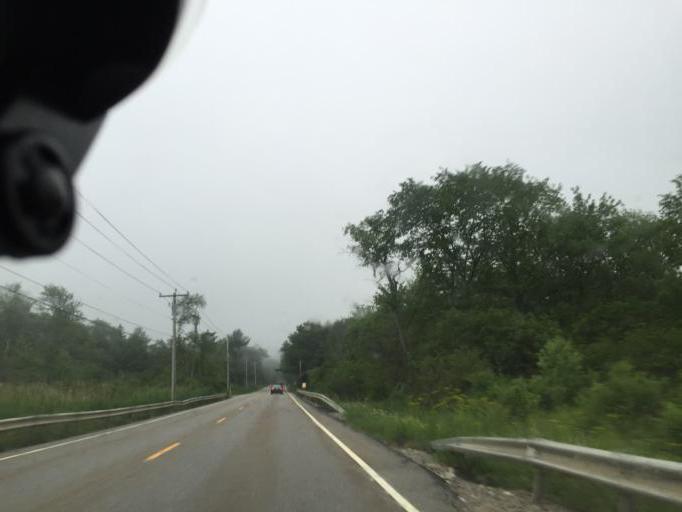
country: US
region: Connecticut
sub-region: Litchfield County
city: West Torrington
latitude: 41.8636
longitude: -73.2474
